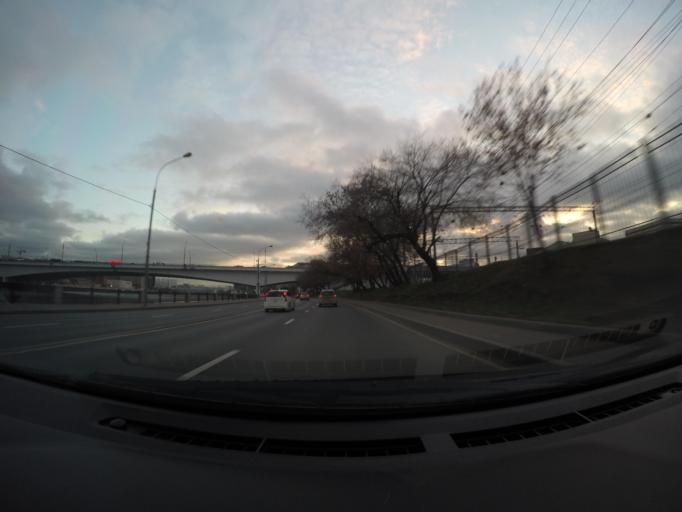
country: RU
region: Moscow
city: Zamoskvorech'ye
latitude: 55.7068
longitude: 37.6276
